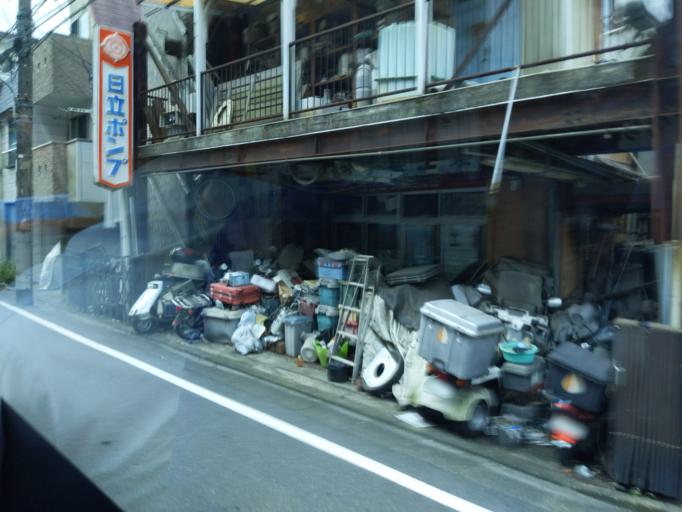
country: JP
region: Kanagawa
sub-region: Kawasaki-shi
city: Kawasaki
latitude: 35.5904
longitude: 139.6881
